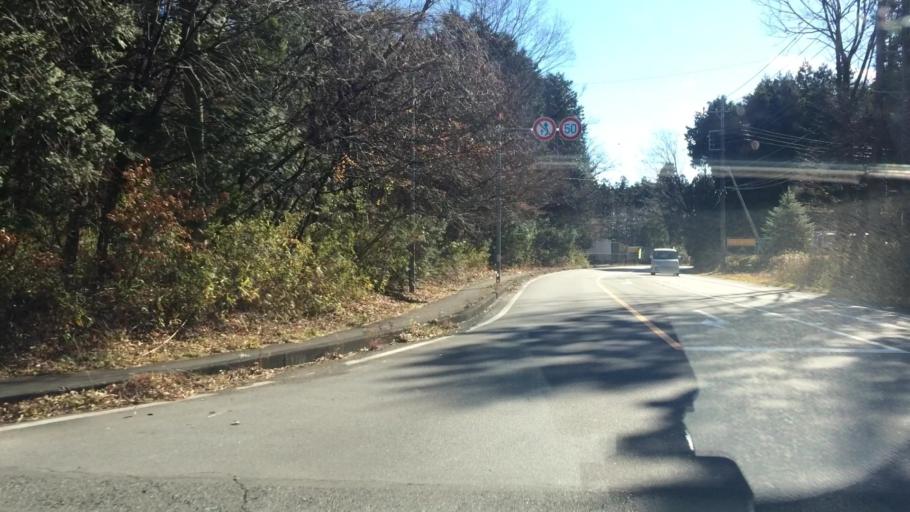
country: JP
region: Tochigi
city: Imaichi
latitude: 36.7558
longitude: 139.7313
